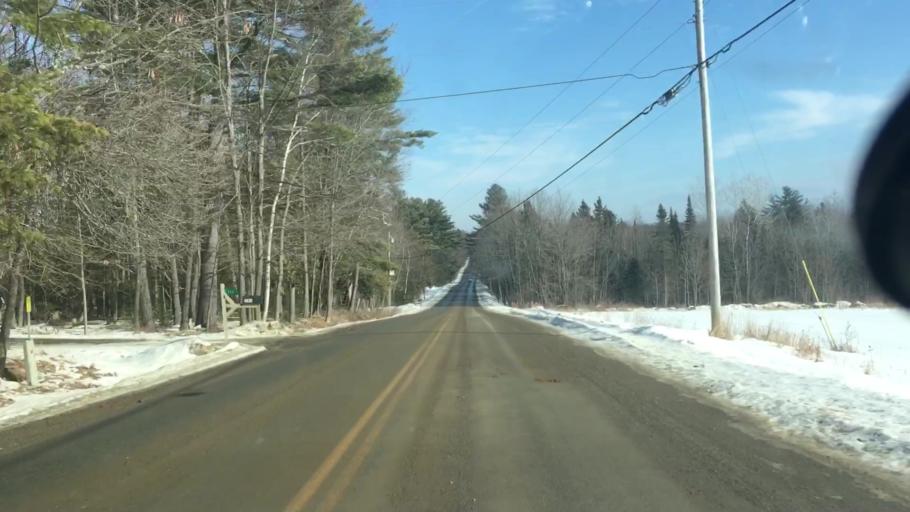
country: US
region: Maine
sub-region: Penobscot County
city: Levant
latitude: 44.8624
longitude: -68.8778
